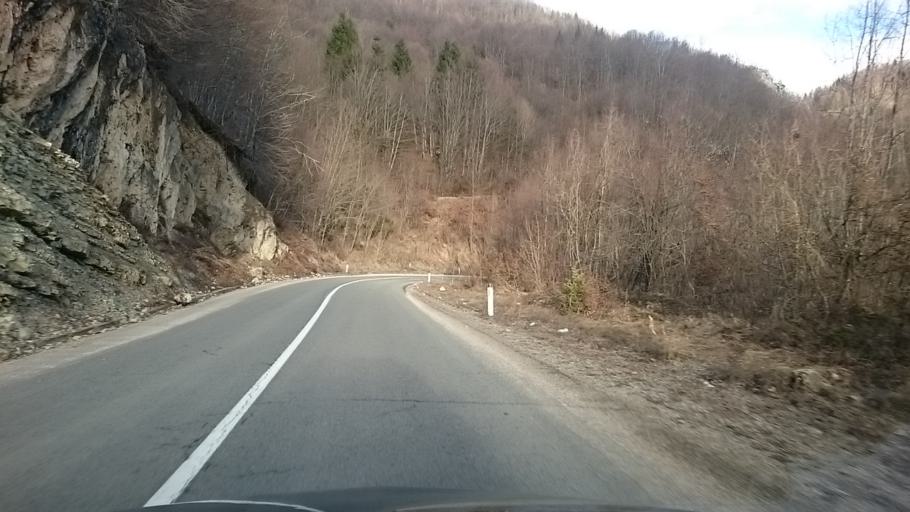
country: BA
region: Republika Srpska
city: Skender Vakuf
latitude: 44.4546
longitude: 17.3712
